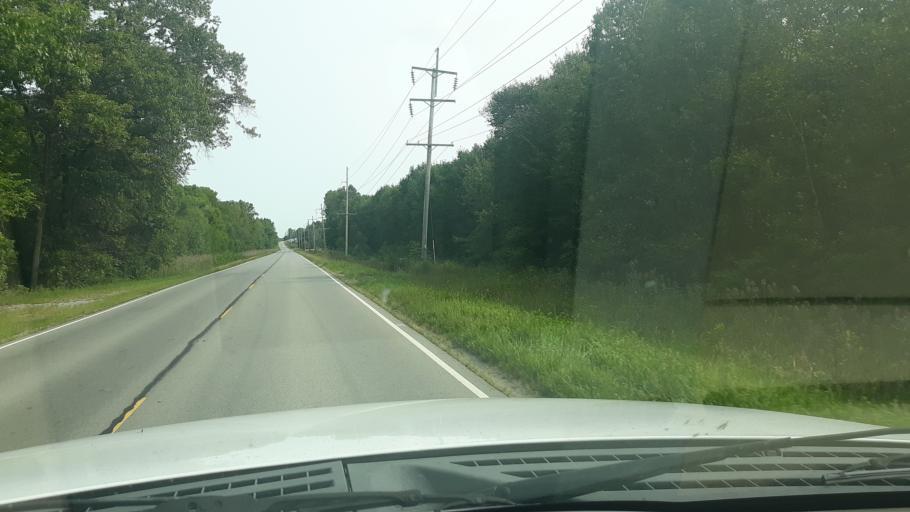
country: US
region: Illinois
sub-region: White County
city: Norris City
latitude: 37.9431
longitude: -88.3421
